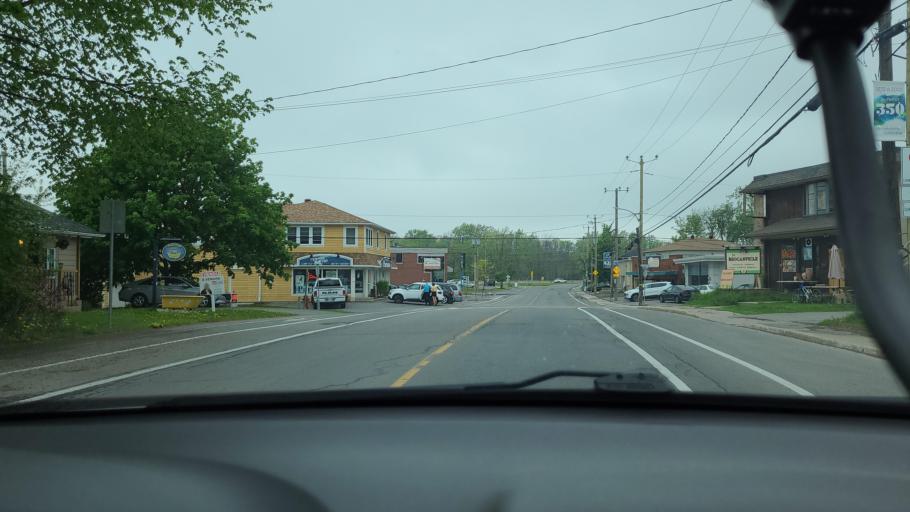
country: CA
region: Quebec
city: Sainte-Anne-de-Bellevue
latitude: 45.3969
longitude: -73.9584
